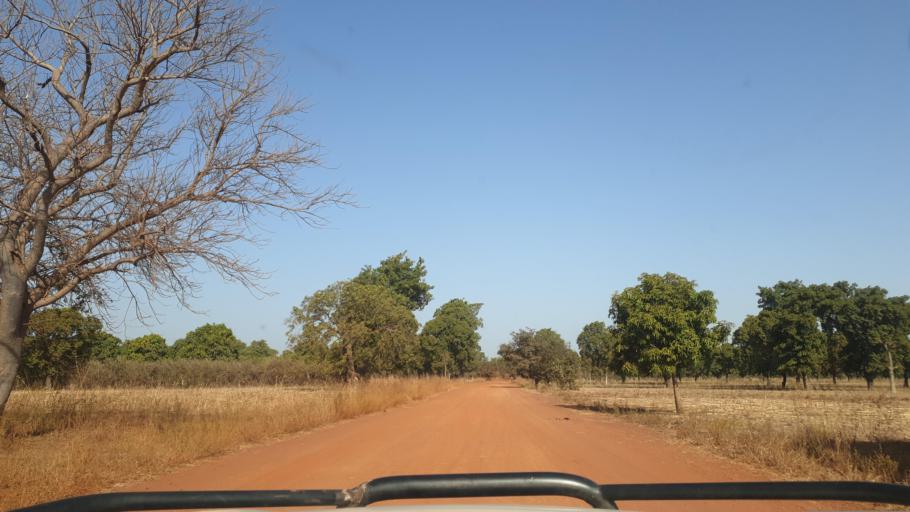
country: ML
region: Sikasso
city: Kolondieba
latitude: 11.7352
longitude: -6.8929
